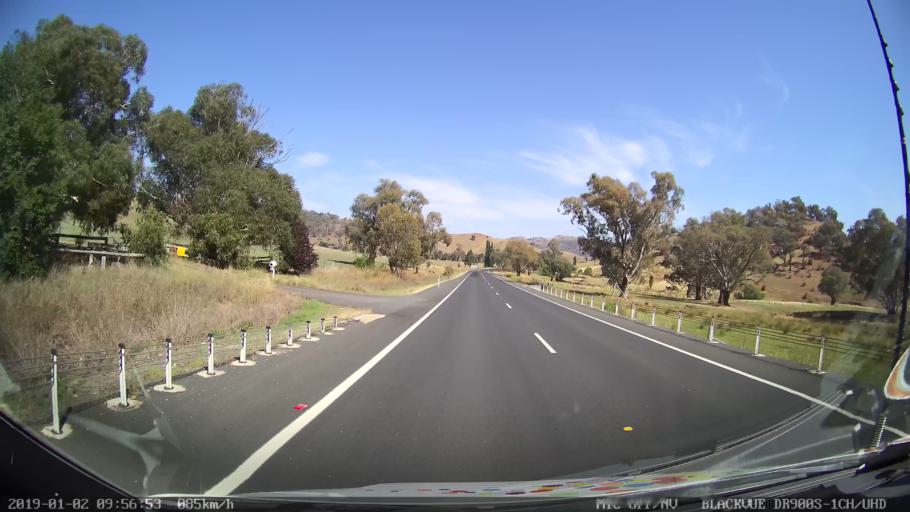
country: AU
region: New South Wales
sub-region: Tumut Shire
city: Tumut
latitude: -35.2114
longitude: 148.1715
